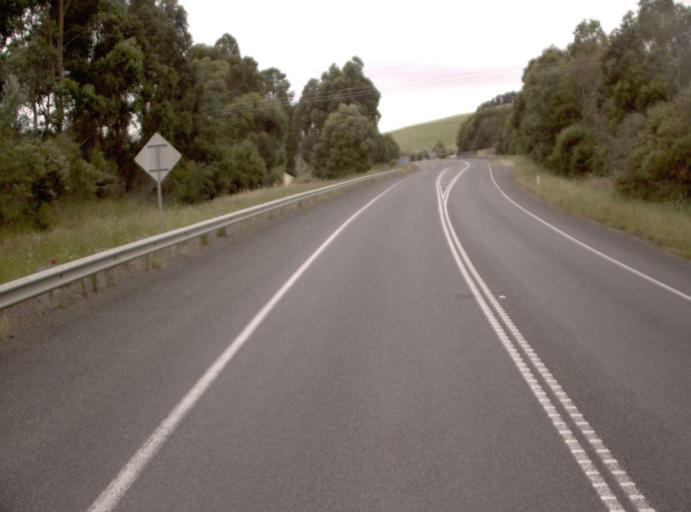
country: AU
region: Victoria
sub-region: Bass Coast
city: North Wonthaggi
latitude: -38.3666
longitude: 145.7077
